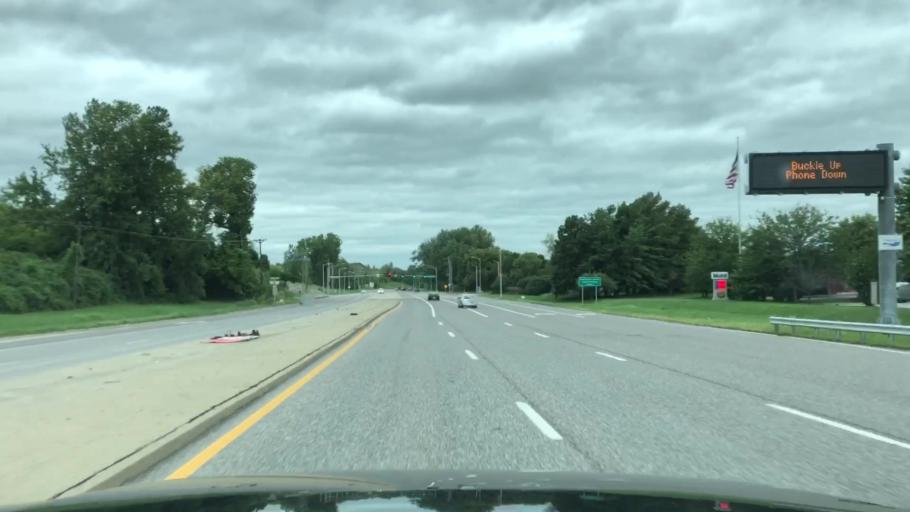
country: US
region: Missouri
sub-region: Saint Charles County
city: Saint Charles
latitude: 38.7509
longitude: -90.4616
